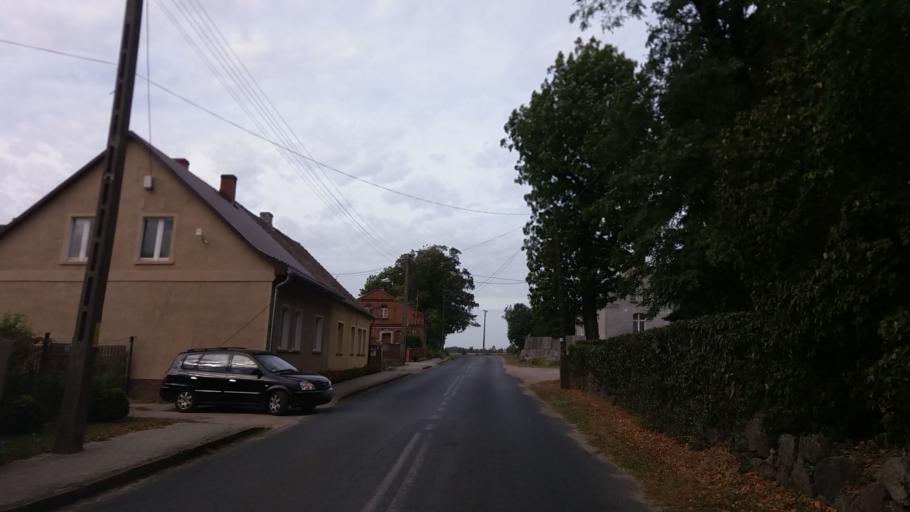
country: PL
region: Lubusz
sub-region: Powiat strzelecko-drezdenecki
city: Strzelce Krajenskie
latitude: 52.9262
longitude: 15.4798
